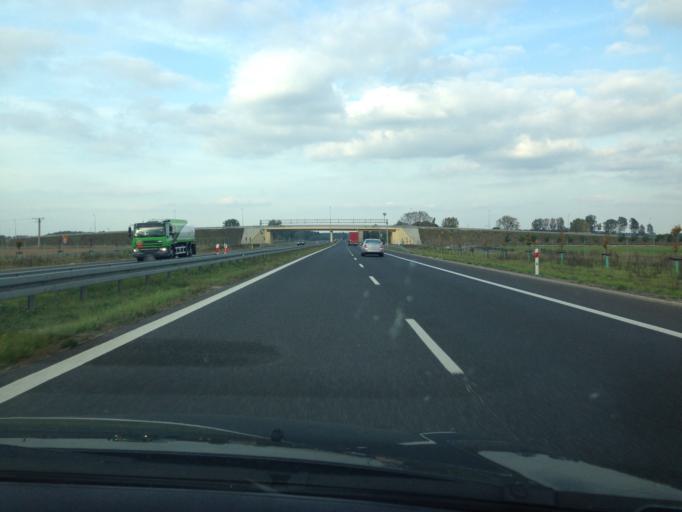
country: PL
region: Greater Poland Voivodeship
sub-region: Powiat gnieznienski
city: Lubowo
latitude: 52.4709
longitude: 17.4070
